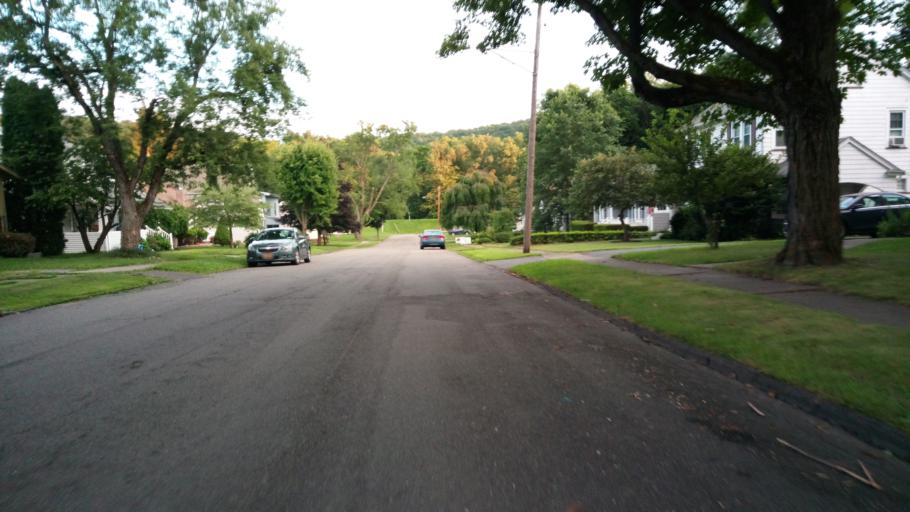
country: US
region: New York
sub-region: Chemung County
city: West Elmira
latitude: 42.0764
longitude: -76.8421
